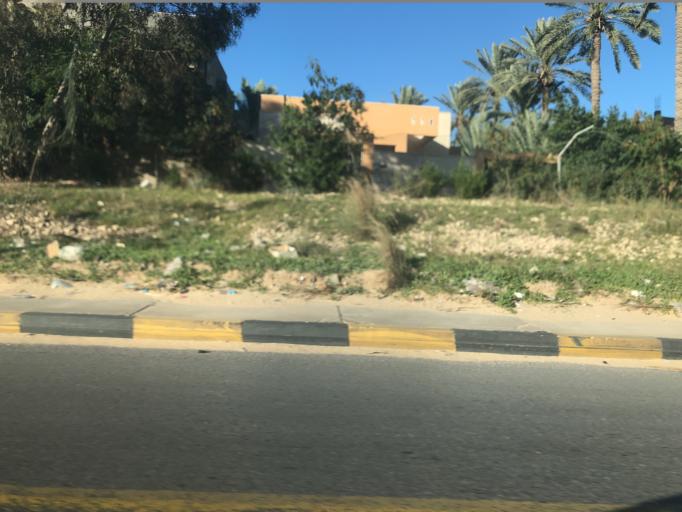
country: LY
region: Tripoli
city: Tripoli
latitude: 32.8689
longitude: 13.2527
